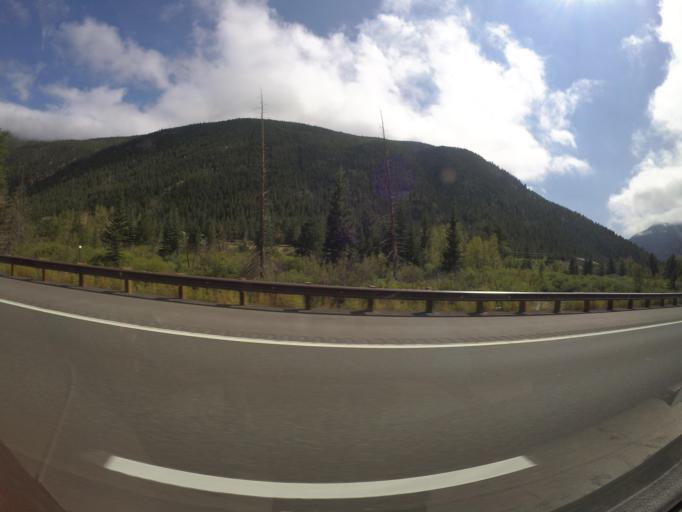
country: US
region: Colorado
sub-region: Clear Creek County
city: Georgetown
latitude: 39.7471
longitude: -105.6768
